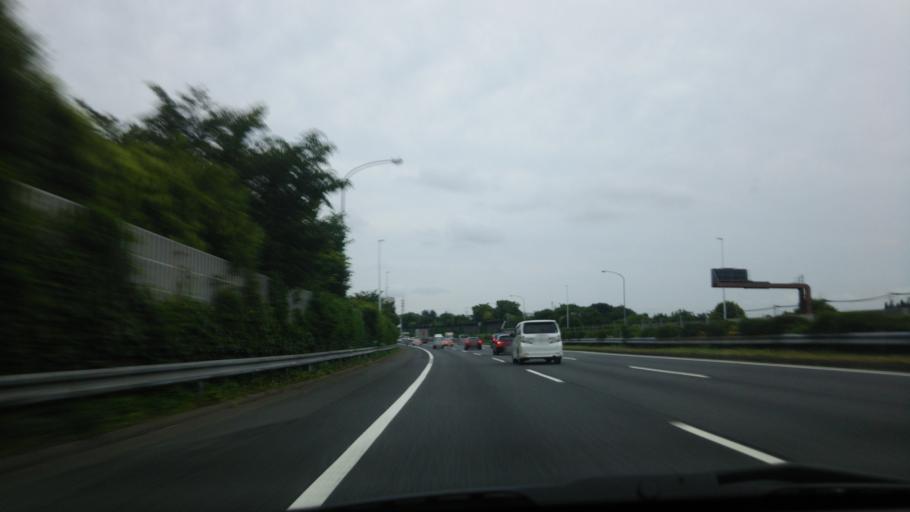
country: JP
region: Kanagawa
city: Minami-rinkan
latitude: 35.4888
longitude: 139.4691
